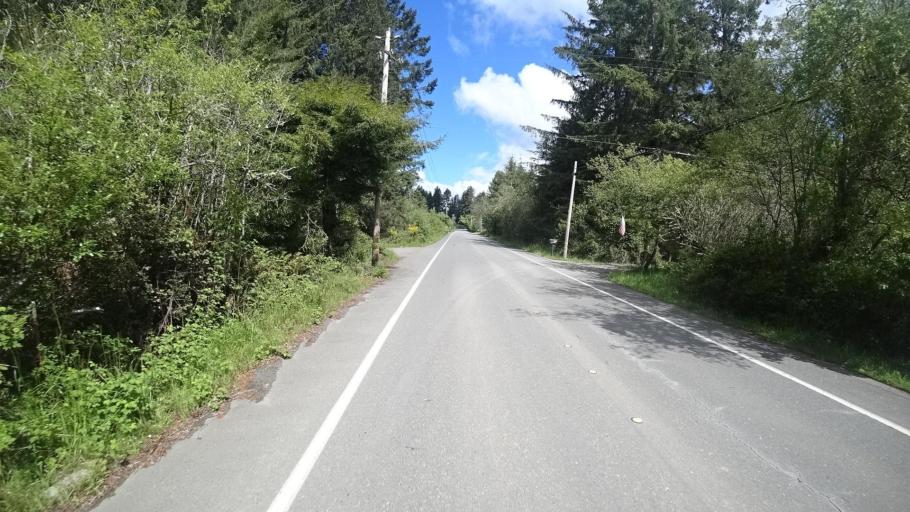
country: US
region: California
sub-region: Humboldt County
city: McKinleyville
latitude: 40.9506
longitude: -124.0323
